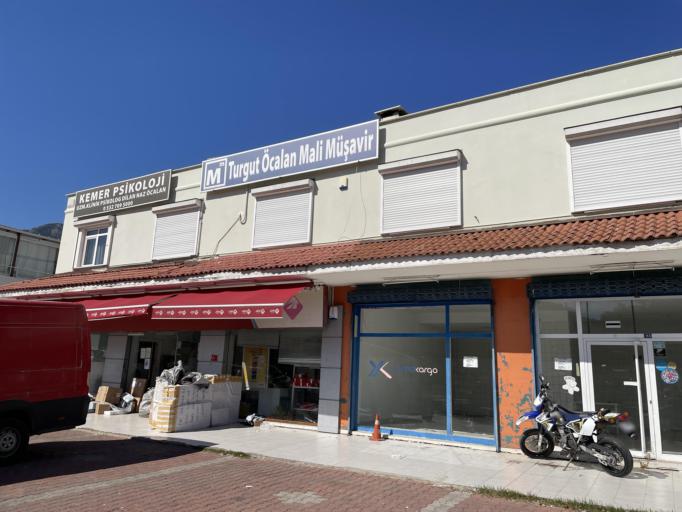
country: TR
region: Antalya
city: Kemer
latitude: 36.6015
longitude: 30.5561
